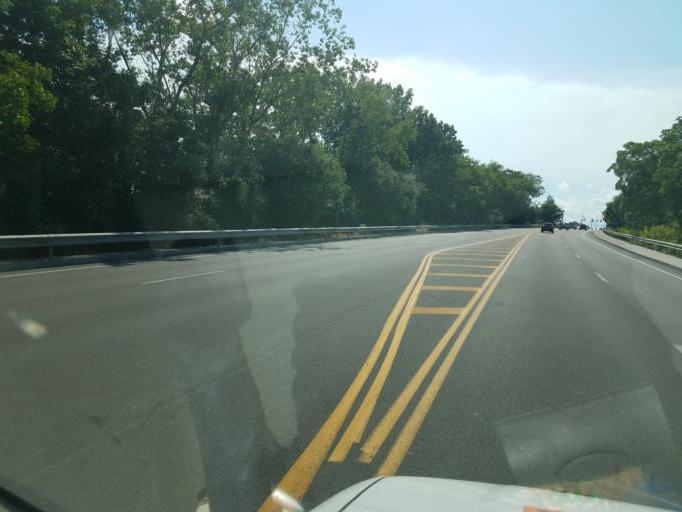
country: US
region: New York
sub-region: Ontario County
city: Geneva
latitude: 42.8565
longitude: -77.0069
